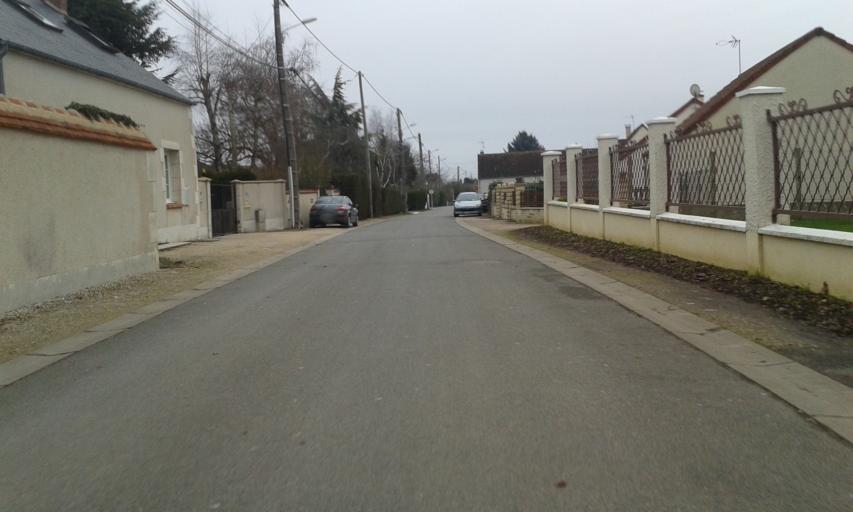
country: FR
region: Centre
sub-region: Departement du Loiret
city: Beaugency
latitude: 47.7992
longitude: 1.6003
